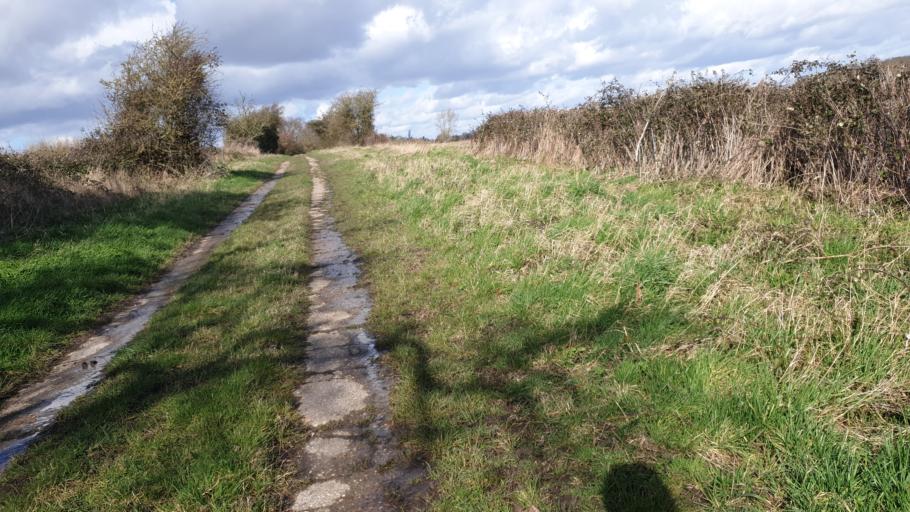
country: GB
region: England
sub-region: Essex
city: Little Clacton
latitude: 51.8423
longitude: 1.1638
